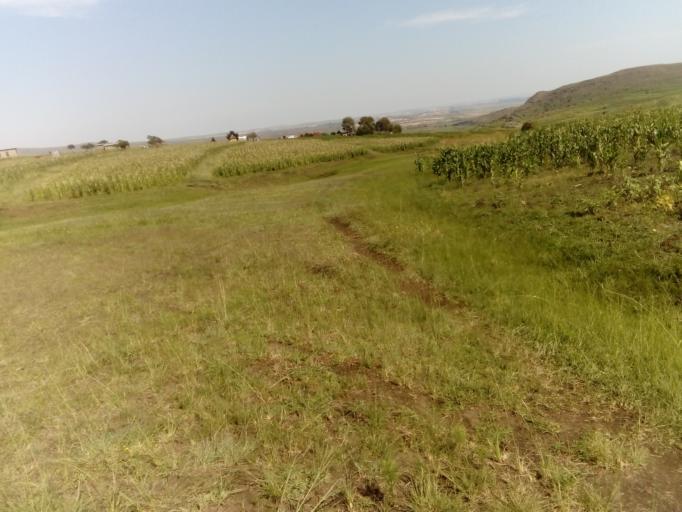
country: LS
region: Berea
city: Teyateyaneng
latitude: -29.2240
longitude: 27.8650
